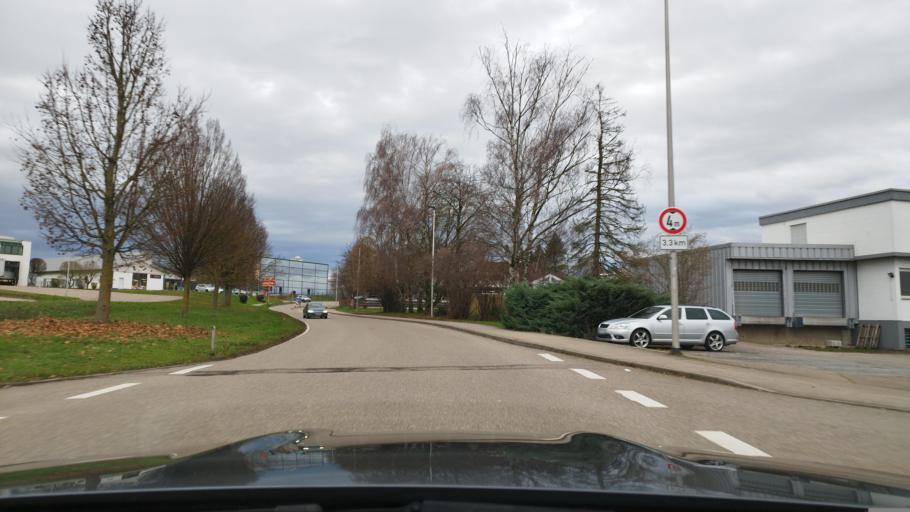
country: DE
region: Baden-Wuerttemberg
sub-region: Regierungsbezirk Stuttgart
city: Kirchberg an der Murr
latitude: 48.9434
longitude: 9.3498
